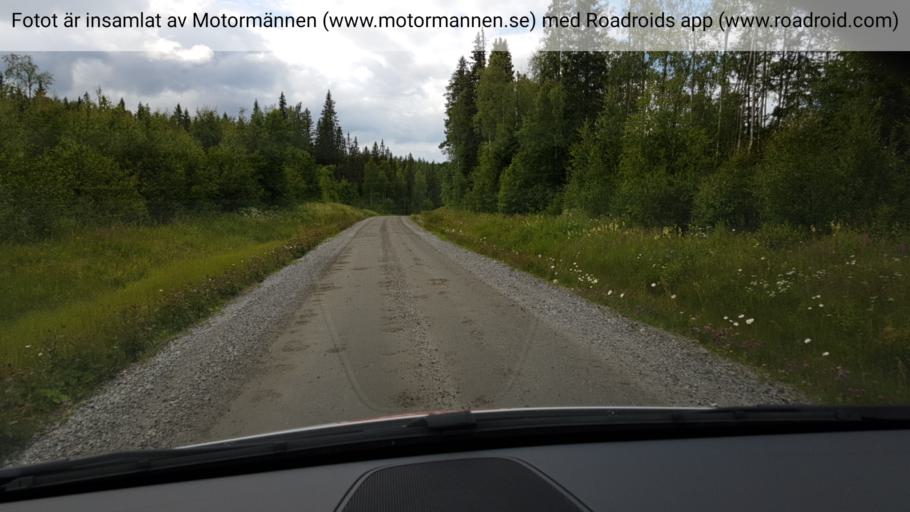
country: SE
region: Vaesterbotten
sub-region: Dorotea Kommun
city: Dorotea
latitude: 63.9219
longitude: 16.1828
